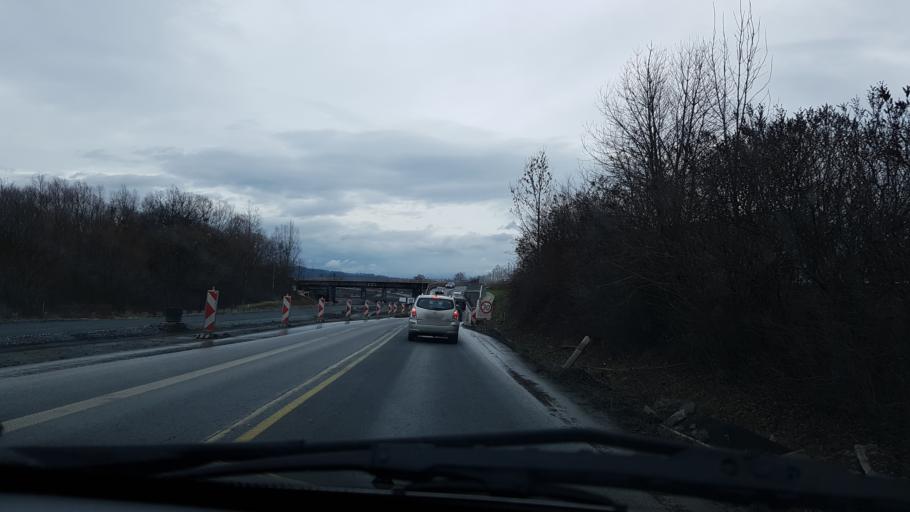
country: CZ
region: Moravskoslezsky
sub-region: Okres Novy Jicin
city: Pribor
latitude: 49.6437
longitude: 18.1567
